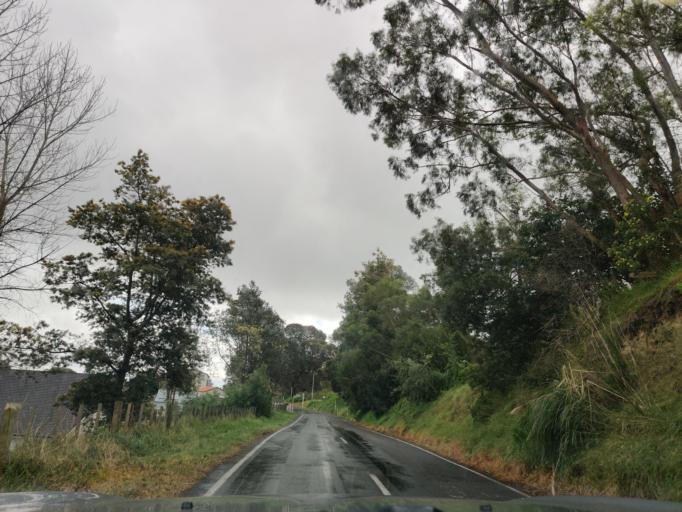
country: NZ
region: Hawke's Bay
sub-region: Hastings District
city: Hastings
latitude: -39.6773
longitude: 176.8959
